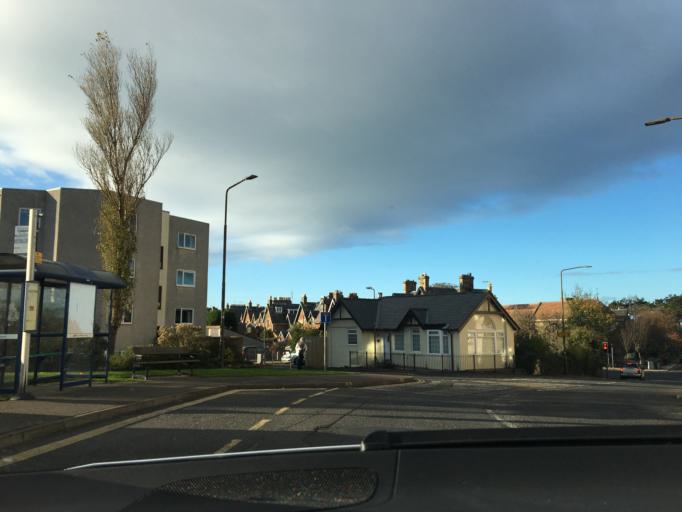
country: GB
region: Scotland
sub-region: East Lothian
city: North Berwick
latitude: 56.0577
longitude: -2.7292
